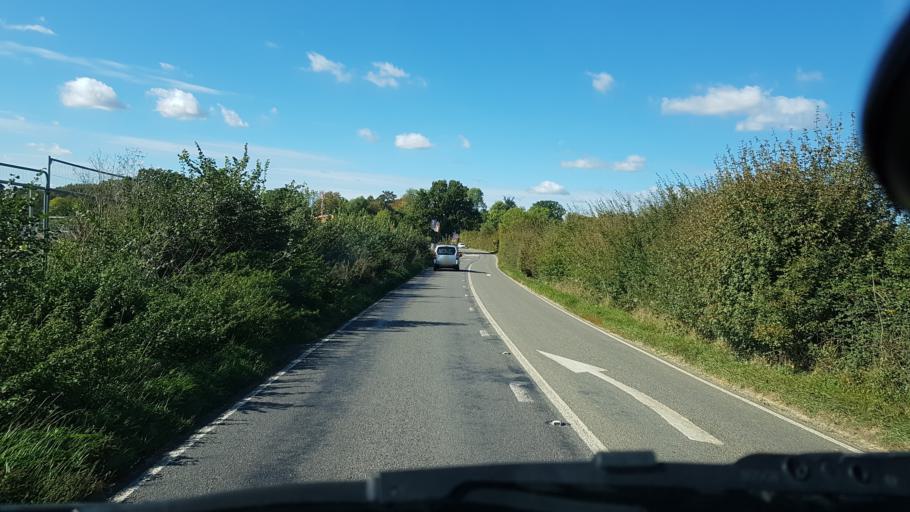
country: GB
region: England
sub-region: West Sussex
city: Billingshurst
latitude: 51.0217
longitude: -0.4406
